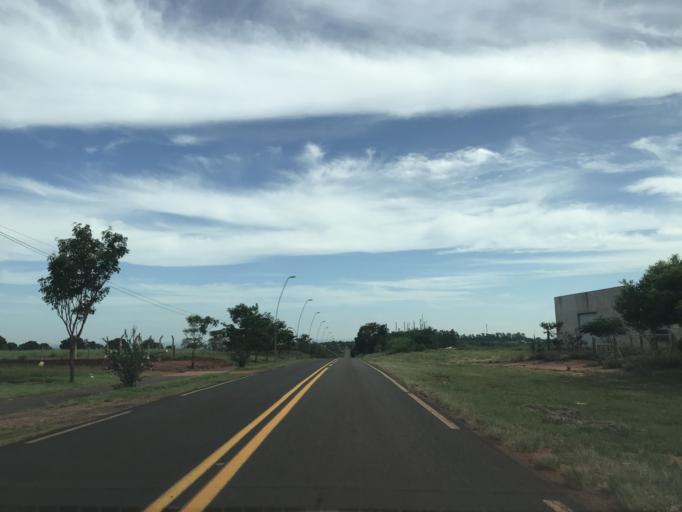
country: BR
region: Parana
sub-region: Terra Rica
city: Terra Rica
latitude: -22.7490
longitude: -52.6250
